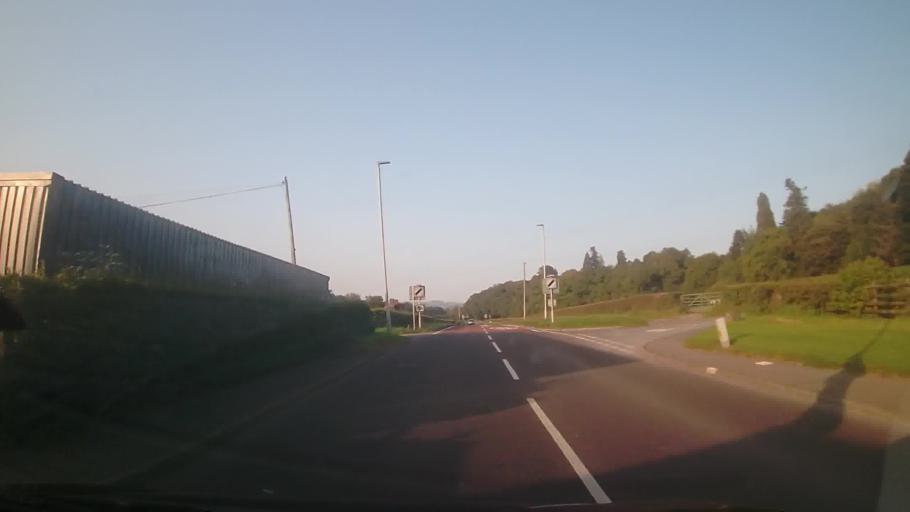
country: GB
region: Wales
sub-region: Sir Powys
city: Mochdre
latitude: 52.4876
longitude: -3.4361
